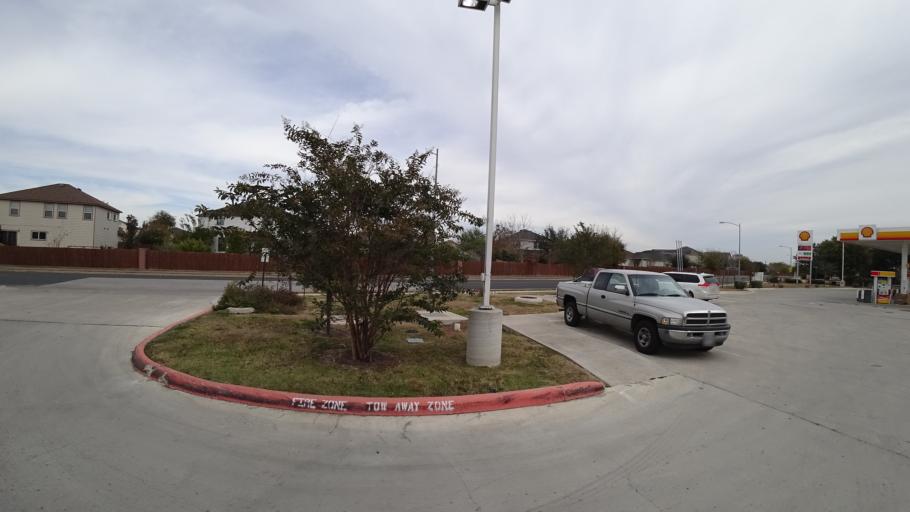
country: US
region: Texas
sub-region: Travis County
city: Onion Creek
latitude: 30.1576
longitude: -97.7446
